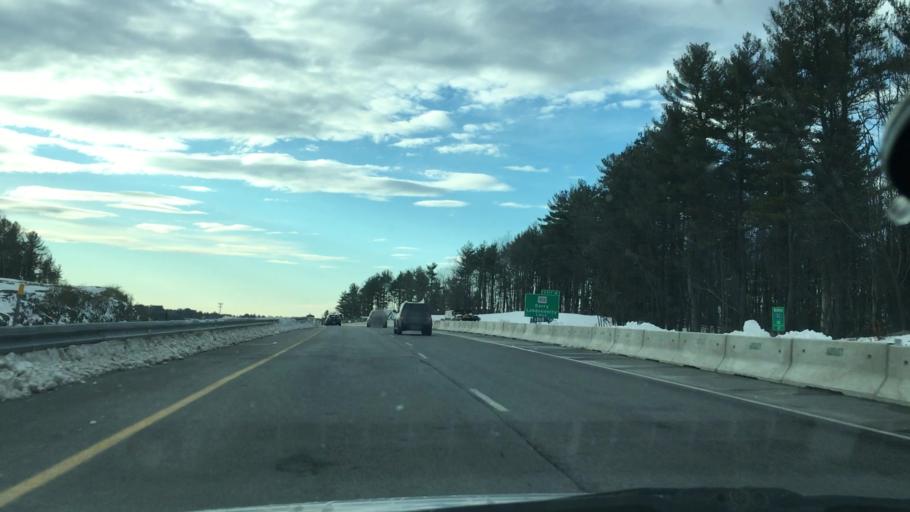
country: US
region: New Hampshire
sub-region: Rockingham County
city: Derry
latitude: 42.8561
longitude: -71.3196
